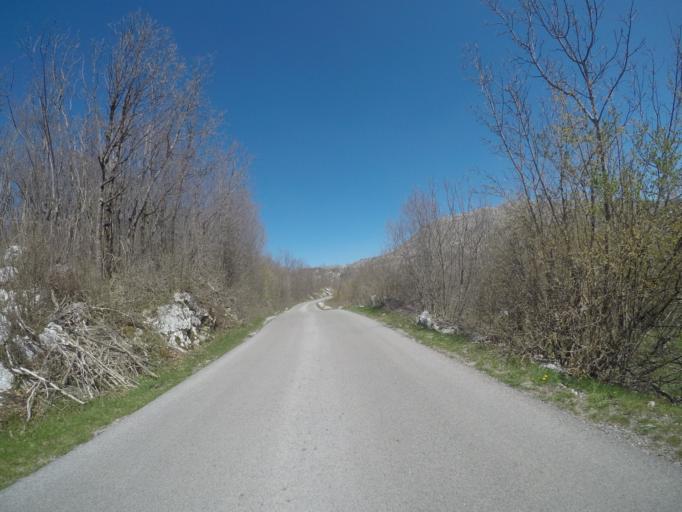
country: ME
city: Dobrota
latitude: 42.4910
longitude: 18.8684
